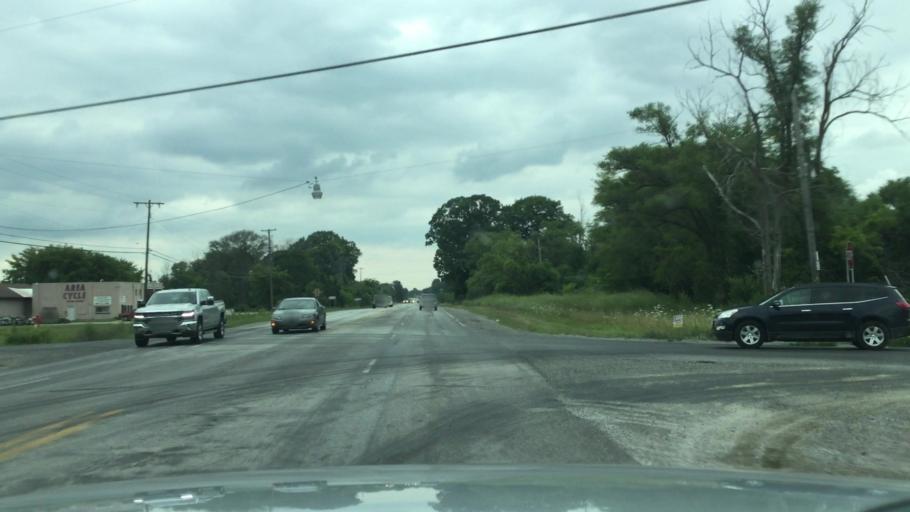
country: US
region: Michigan
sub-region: Saginaw County
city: Bridgeport
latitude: 43.3214
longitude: -83.8231
